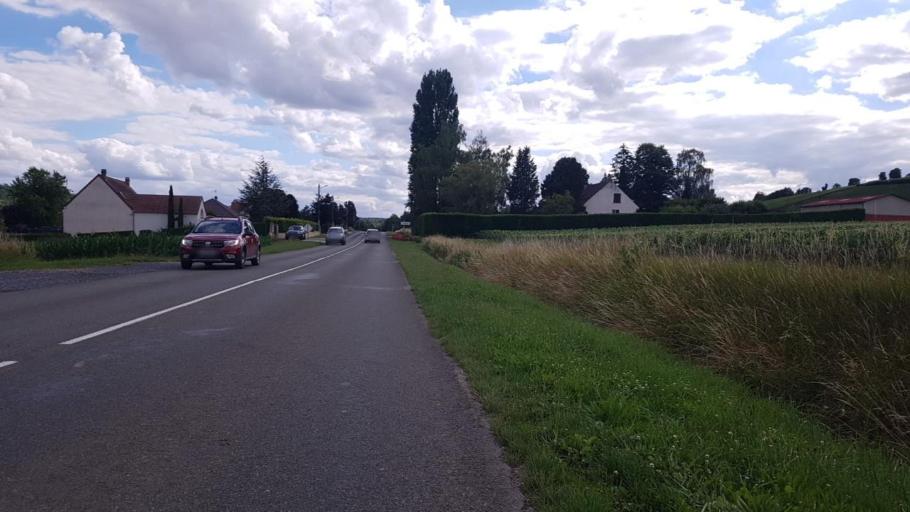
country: FR
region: Picardie
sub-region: Departement de l'Aisne
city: Crezancy
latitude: 49.0536
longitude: 3.4715
